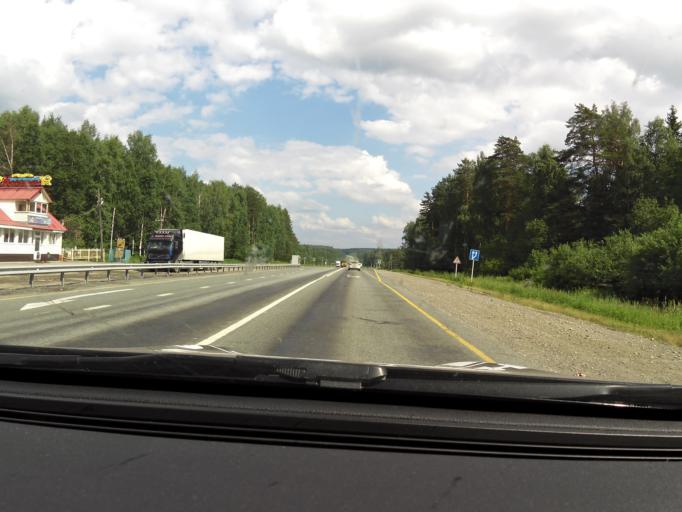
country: RU
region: Sverdlovsk
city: Bisert'
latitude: 56.8320
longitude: 58.9500
